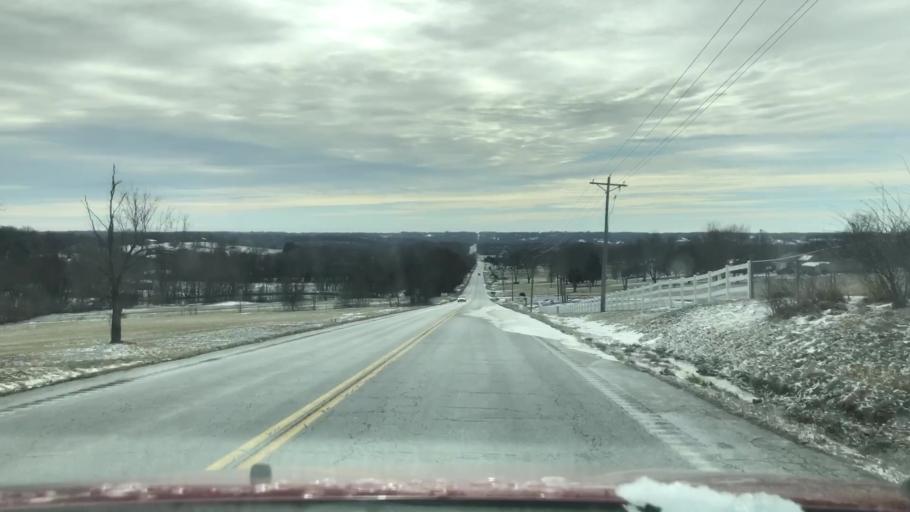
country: US
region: Missouri
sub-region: Jackson County
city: Lone Jack
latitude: 38.9300
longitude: -94.1327
